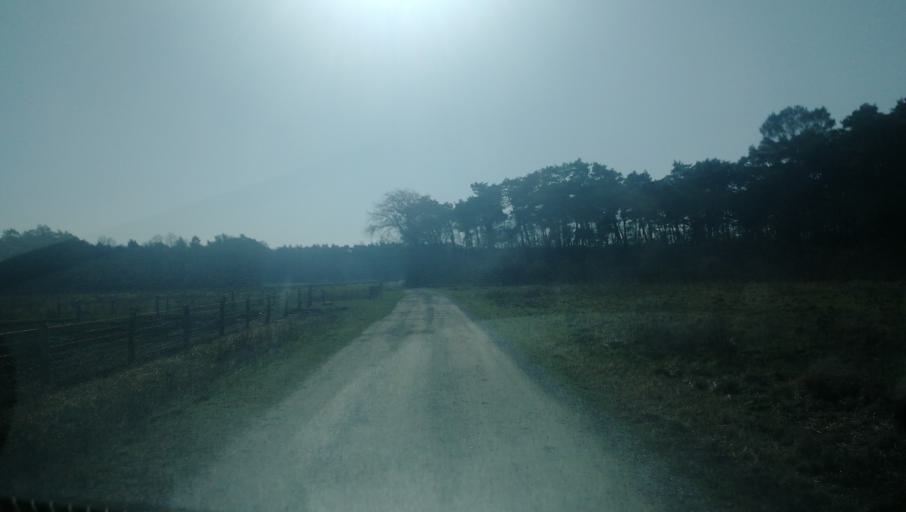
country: NL
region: Limburg
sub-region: Gemeente Venlo
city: Tegelen
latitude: 51.3807
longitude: 6.0978
